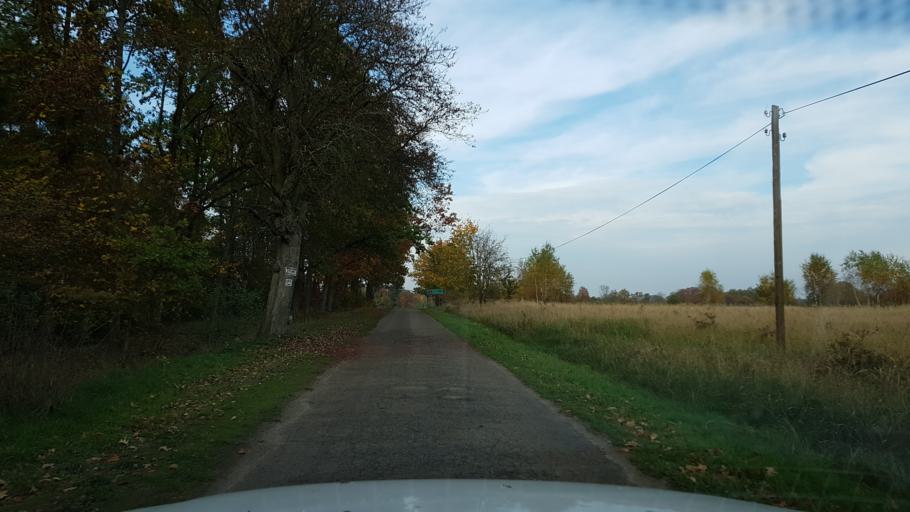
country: PL
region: West Pomeranian Voivodeship
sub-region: Powiat lobeski
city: Wegorzyno
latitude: 53.5143
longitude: 15.4965
